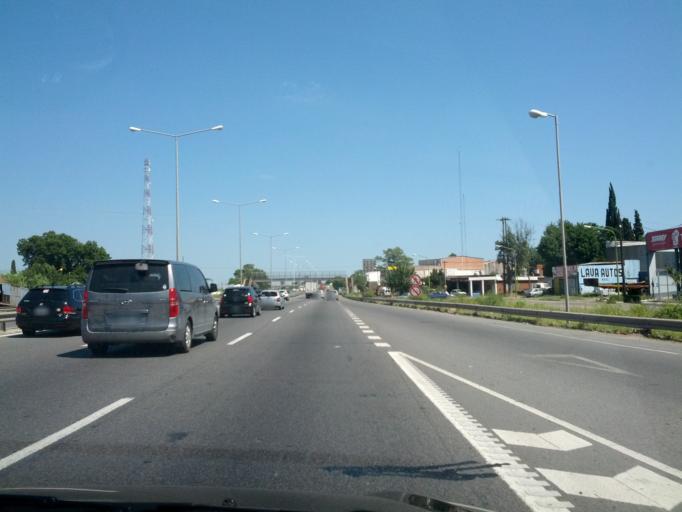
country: AR
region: Buenos Aires
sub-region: Partido de Campana
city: Campana
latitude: -34.1806
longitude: -58.9632
